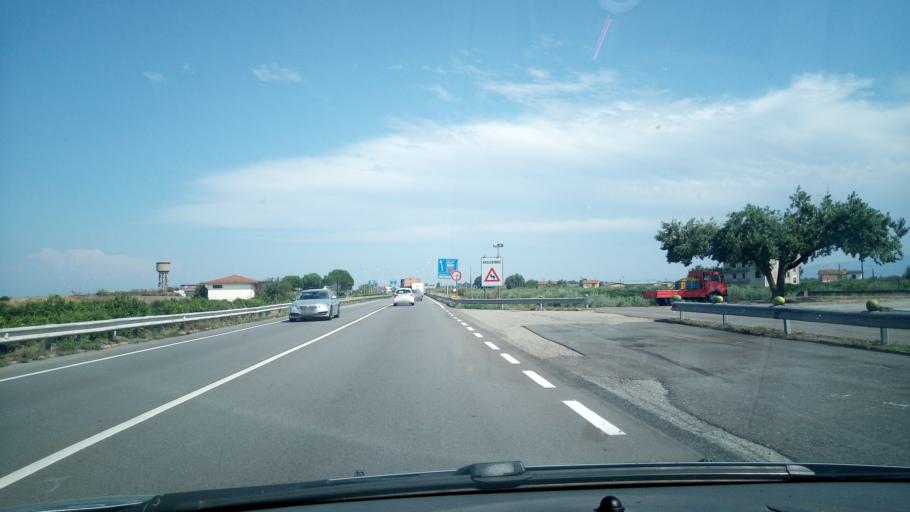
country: IT
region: Calabria
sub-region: Provincia di Cosenza
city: Sibari
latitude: 39.7232
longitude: 16.4404
